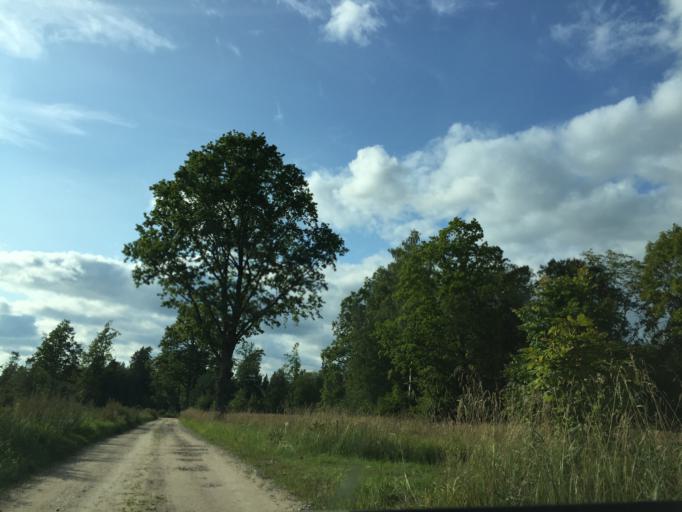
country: LV
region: Kegums
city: Kegums
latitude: 56.8121
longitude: 24.7506
